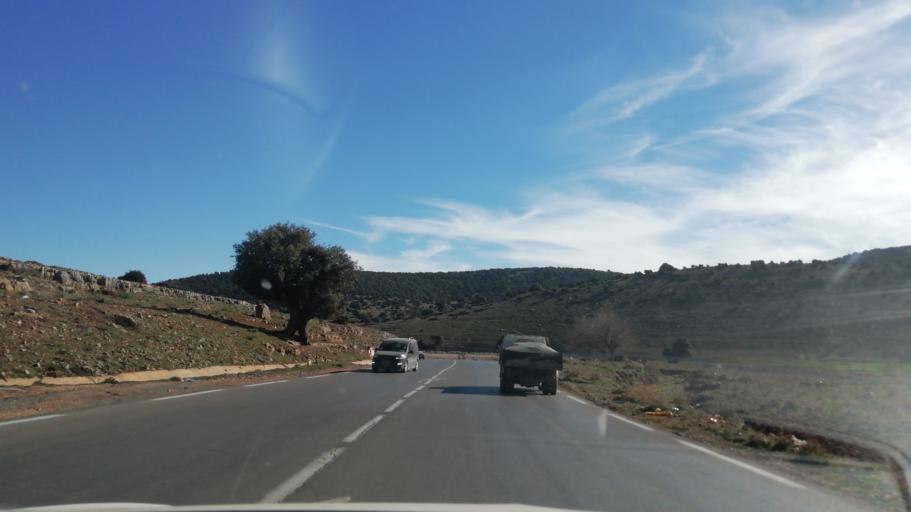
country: DZ
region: Tlemcen
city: Sebdou
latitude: 34.7178
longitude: -1.3368
